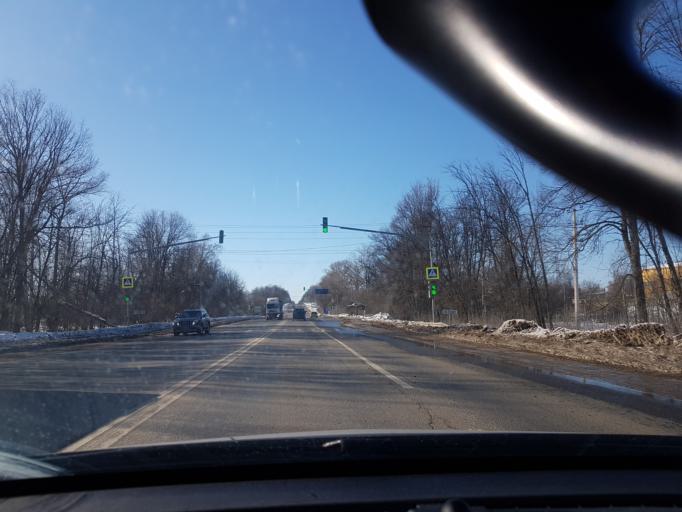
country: RU
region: Moskovskaya
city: Istra
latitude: 55.9079
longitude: 36.7991
